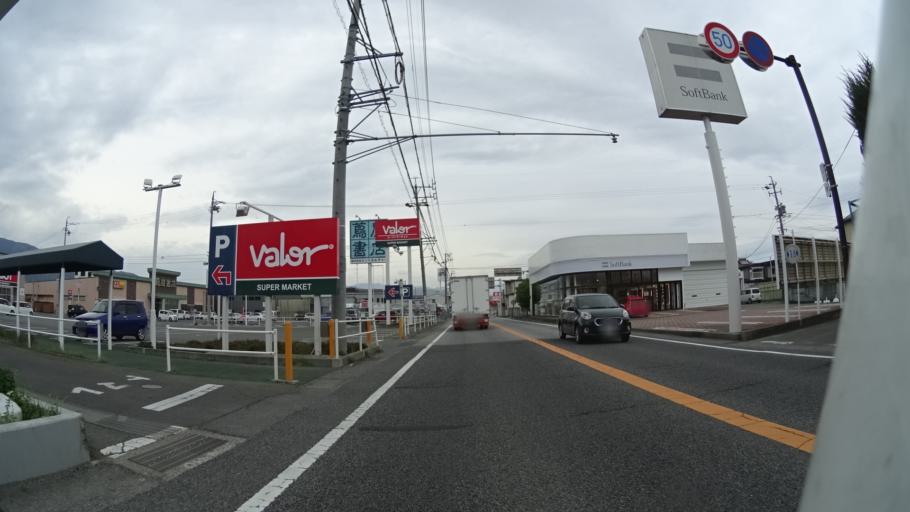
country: JP
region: Nagano
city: Nagano-shi
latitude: 36.5330
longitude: 138.1231
